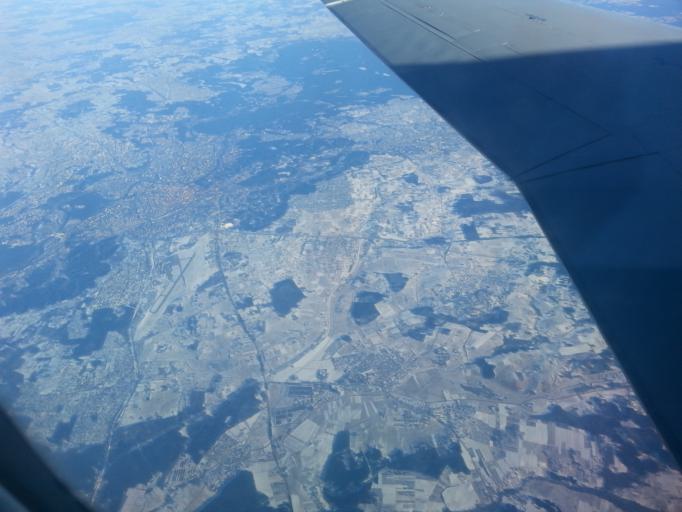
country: LT
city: Skaidiskes
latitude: 54.5242
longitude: 25.3142
